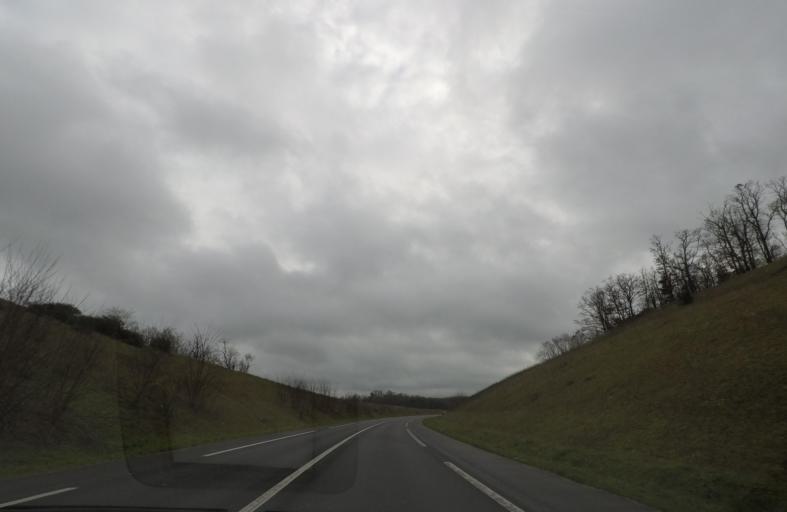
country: FR
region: Centre
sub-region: Departement du Loir-et-Cher
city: Naveil
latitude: 47.7782
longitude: 1.0276
